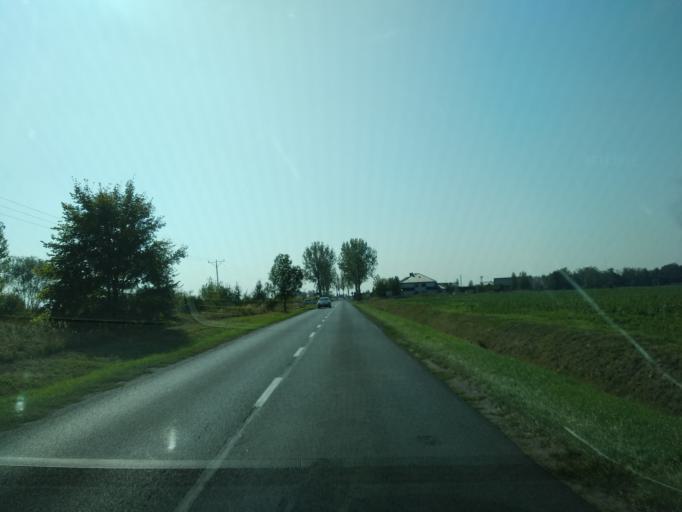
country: PL
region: Lower Silesian Voivodeship
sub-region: Powiat wroclawski
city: Zerniki Wroclawskie
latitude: 51.0259
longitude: 17.0344
